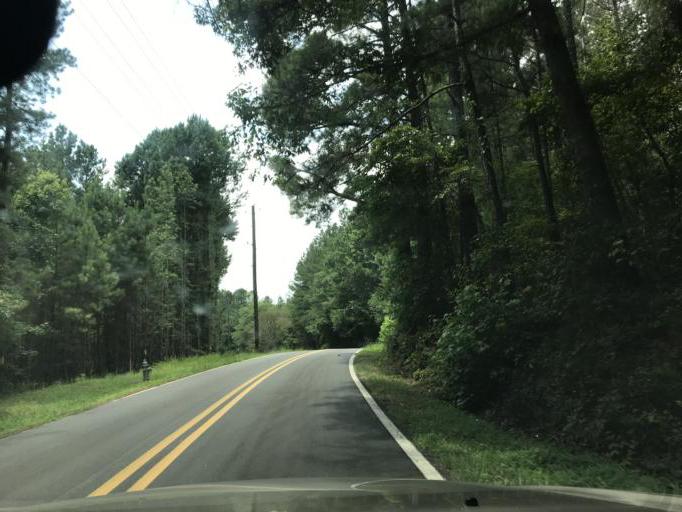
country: US
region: Georgia
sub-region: Dawson County
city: Dawsonville
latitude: 34.3264
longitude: -84.2140
